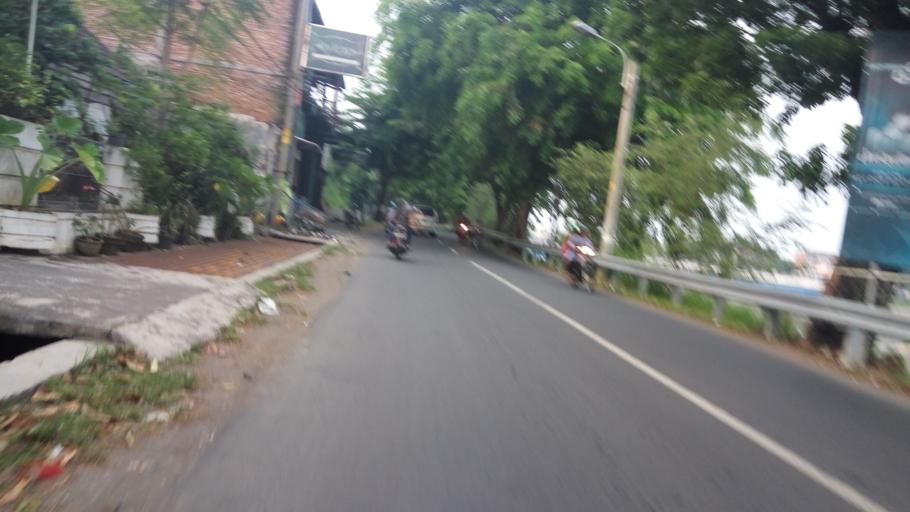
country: ID
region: Central Java
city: Semarang
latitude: -6.9925
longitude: 110.4017
